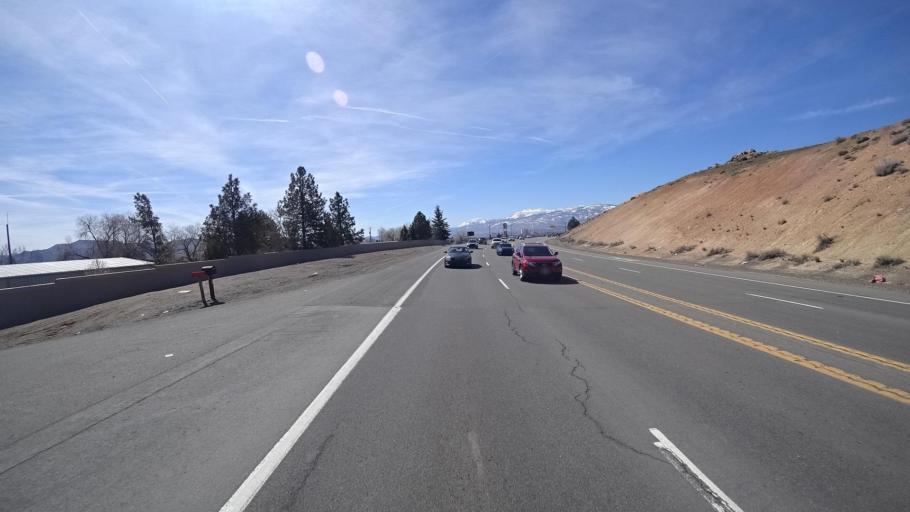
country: US
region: Nevada
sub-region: Washoe County
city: Sparks
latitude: 39.5656
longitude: -119.7472
